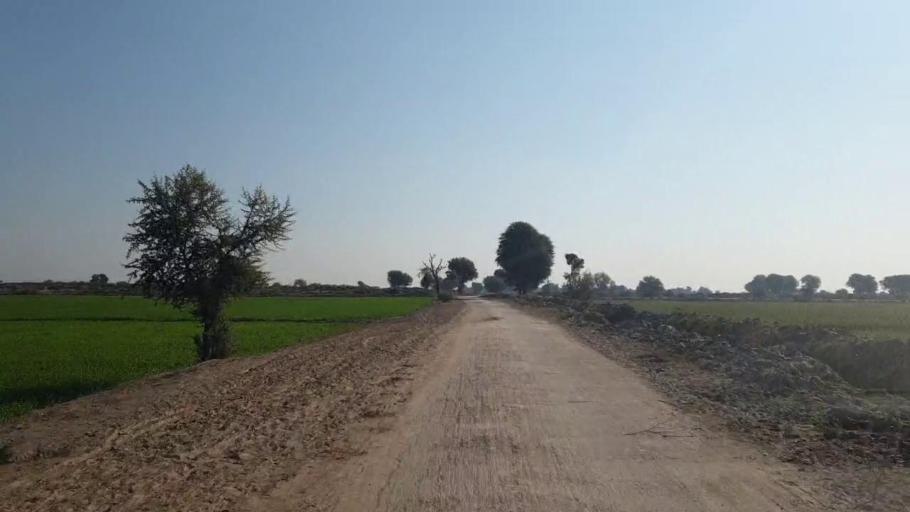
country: PK
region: Sindh
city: Shahpur Chakar
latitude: 26.0895
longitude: 68.6454
